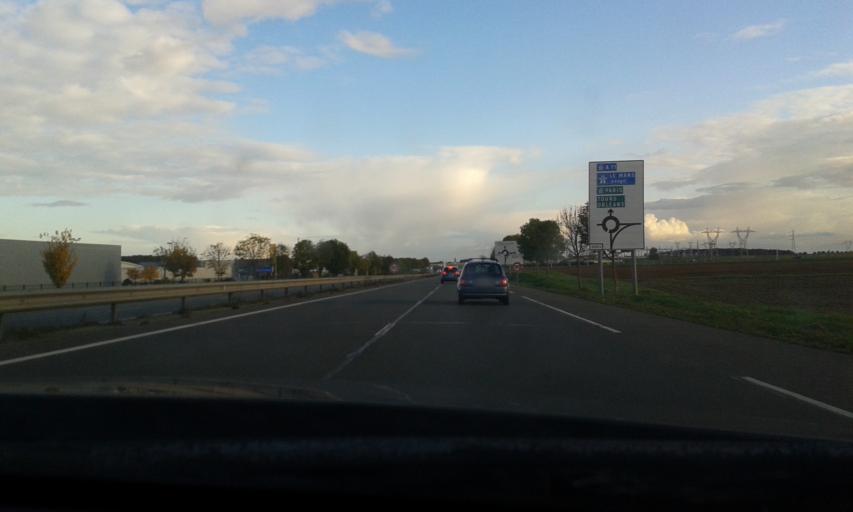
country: FR
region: Centre
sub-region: Departement d'Eure-et-Loir
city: Luce
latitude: 48.4212
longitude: 1.4403
